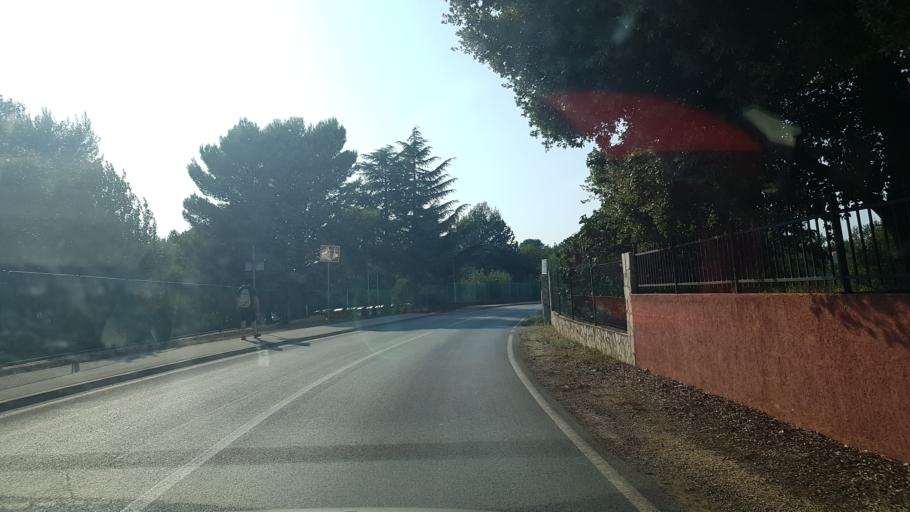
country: HR
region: Istarska
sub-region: Grad Rovinj
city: Rovinj
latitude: 45.1067
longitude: 13.6250
